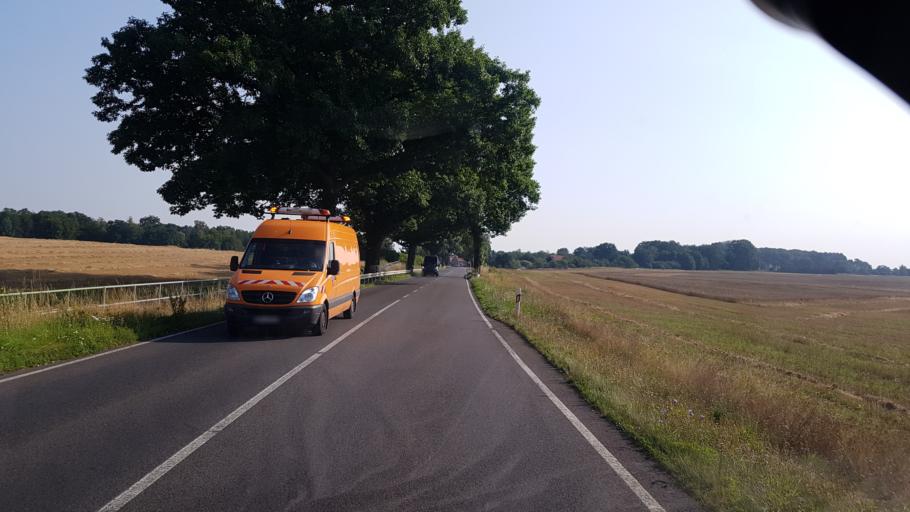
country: DE
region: Brandenburg
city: Kolkwitz
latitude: 51.6950
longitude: 14.2745
